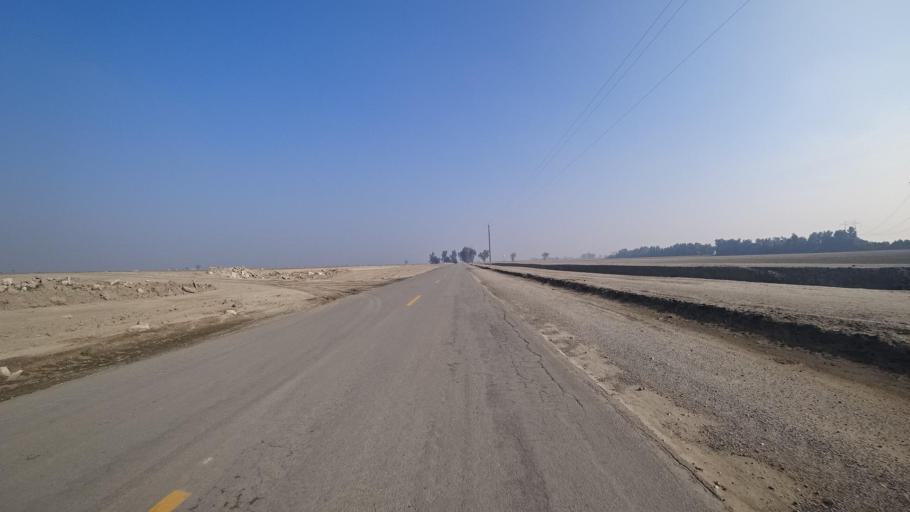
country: US
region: California
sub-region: Kern County
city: Greenfield
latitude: 35.1511
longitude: -119.0175
